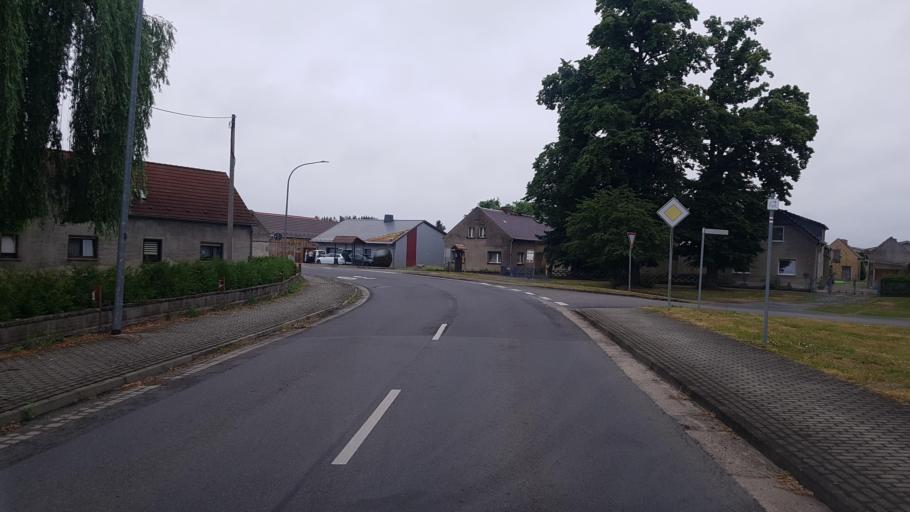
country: DE
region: Brandenburg
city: Hermsdorf
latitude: 51.3991
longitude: 13.8515
